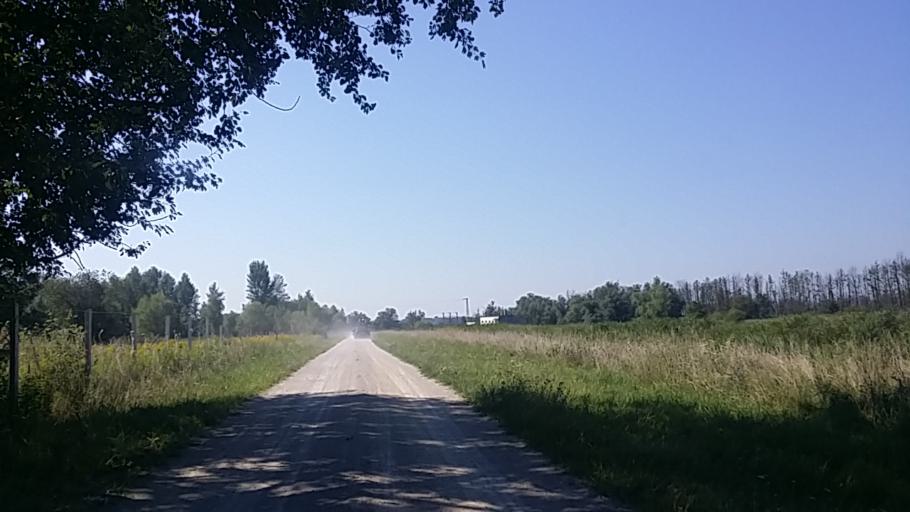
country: HU
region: Zala
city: Sarmellek
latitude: 46.6975
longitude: 17.2366
